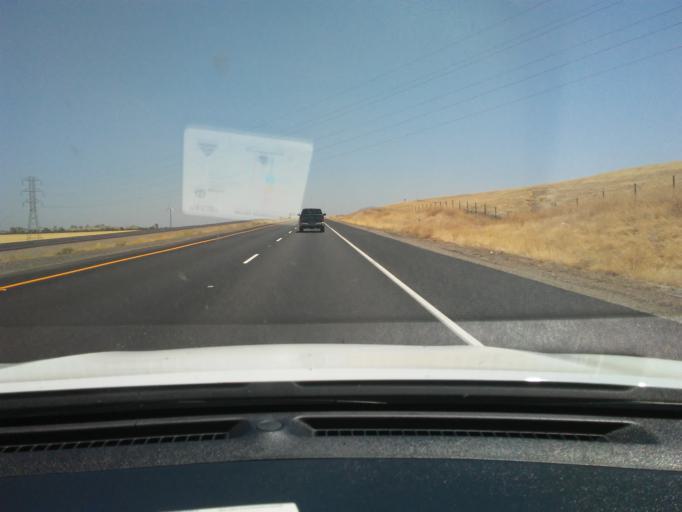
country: US
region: California
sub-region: San Joaquin County
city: Tracy
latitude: 37.6246
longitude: -121.3791
